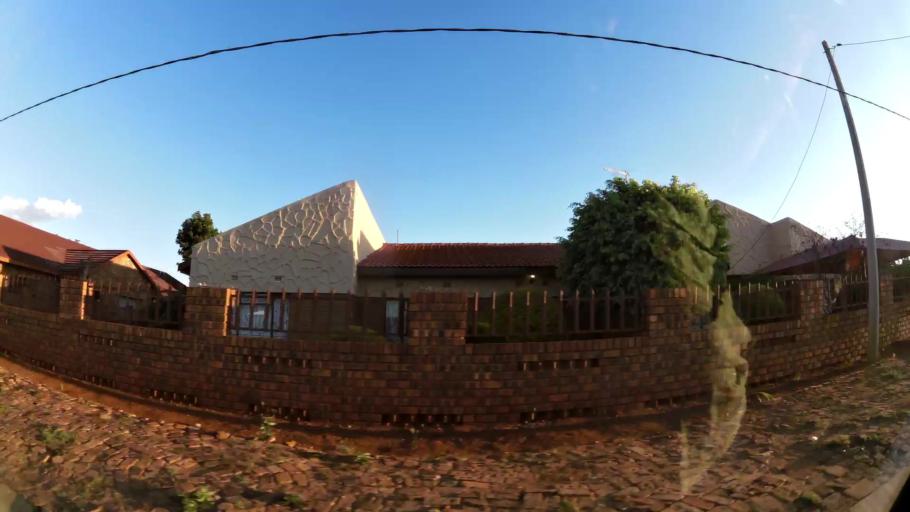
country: ZA
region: Limpopo
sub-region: Waterberg District Municipality
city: Mokopane
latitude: -24.1387
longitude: 28.9837
